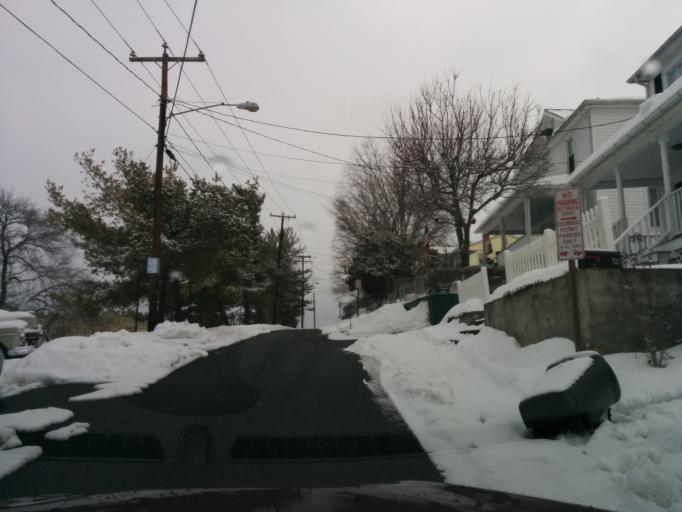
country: US
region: Virginia
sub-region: City of Lexington
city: Lexington
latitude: 37.7878
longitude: -79.4366
